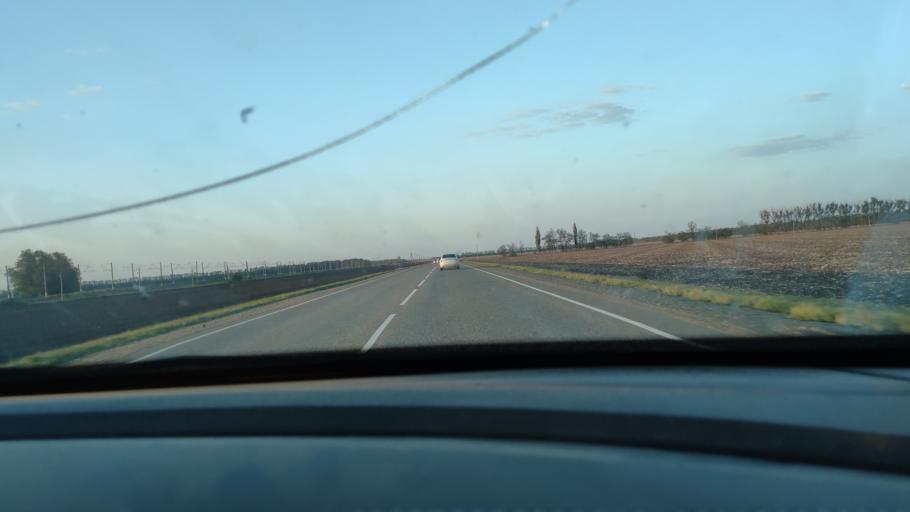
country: RU
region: Krasnodarskiy
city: Novominskaya
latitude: 46.3565
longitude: 38.9651
